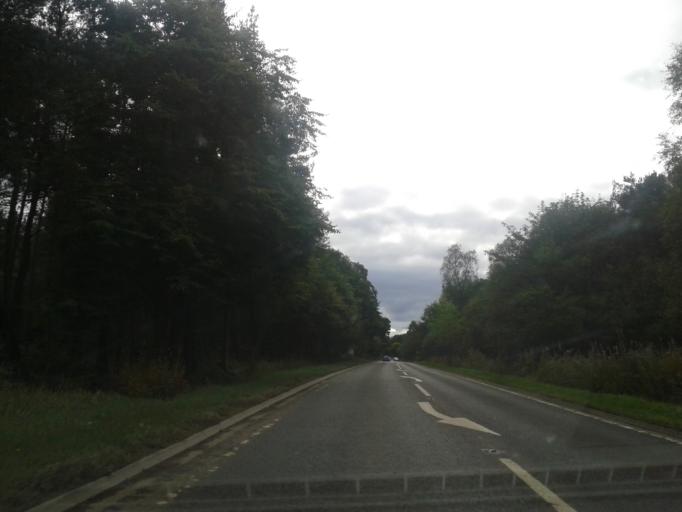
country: GB
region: Scotland
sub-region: Fife
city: Ladybank
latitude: 56.2928
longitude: -3.1268
